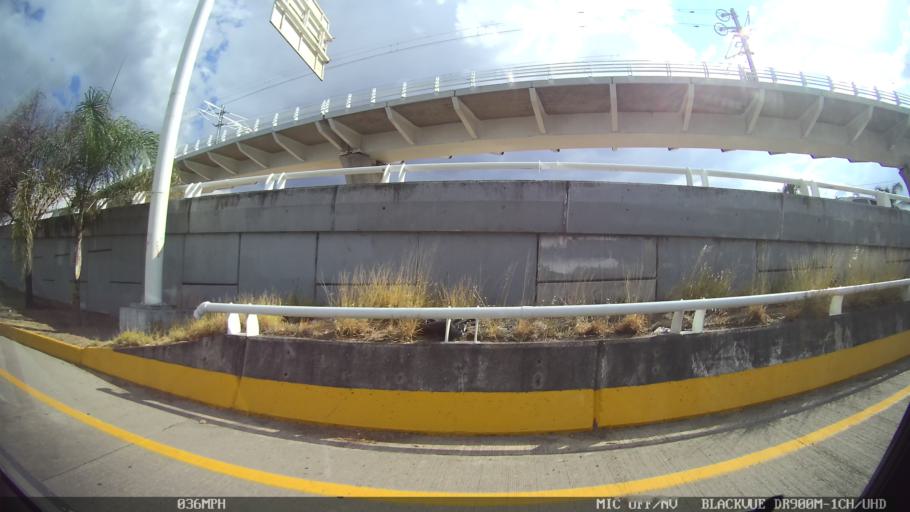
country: MX
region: Jalisco
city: Tlaquepaque
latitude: 20.6299
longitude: -103.2938
